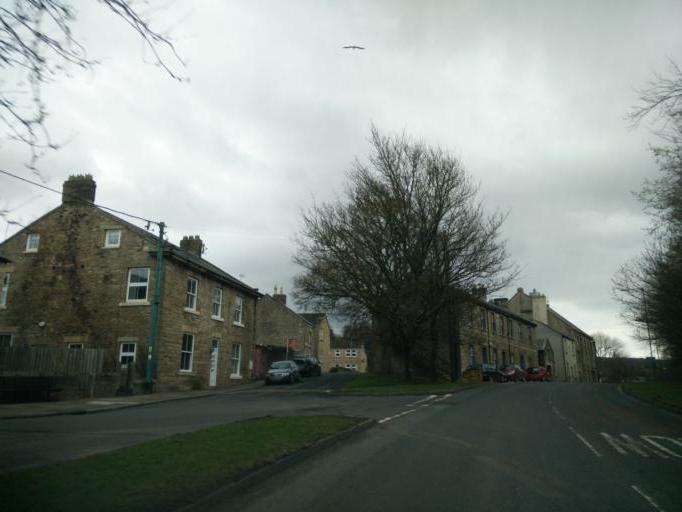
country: GB
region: England
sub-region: County Durham
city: Stanhope
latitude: 54.7491
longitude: -2.0121
